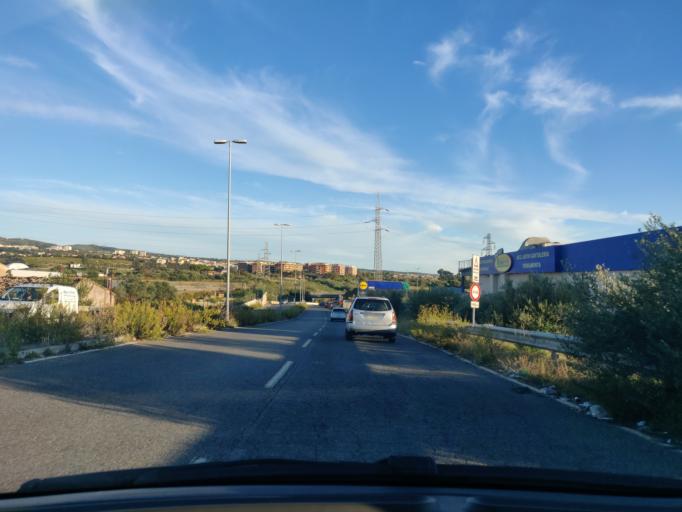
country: IT
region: Latium
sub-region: Citta metropolitana di Roma Capitale
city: Civitavecchia
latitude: 42.1080
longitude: 11.7871
